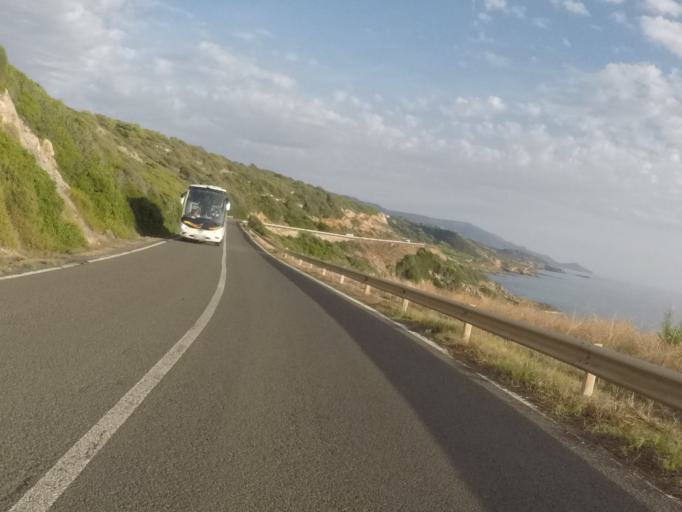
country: IT
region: Sardinia
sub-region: Provincia di Sassari
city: Alghero
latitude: 40.5306
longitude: 8.3274
